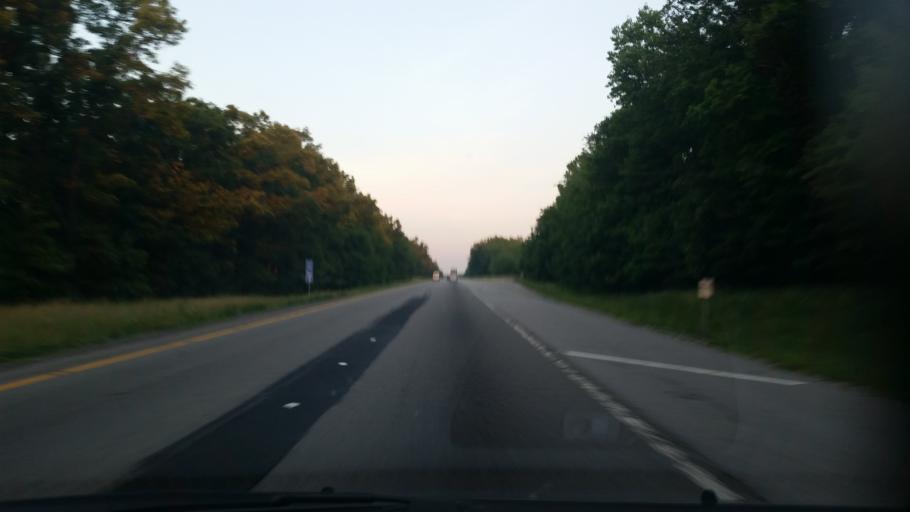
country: US
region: Tennessee
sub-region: Putnam County
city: Monterey
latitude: 36.0819
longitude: -85.2138
